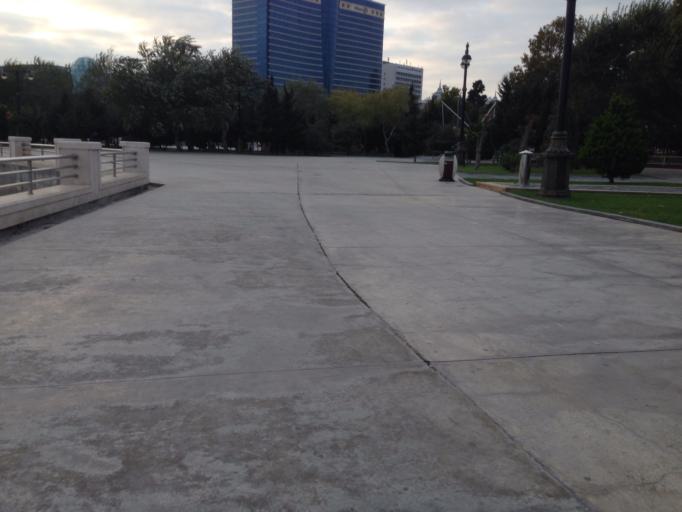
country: AZ
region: Baki
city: Baku
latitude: 40.3708
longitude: 49.8537
